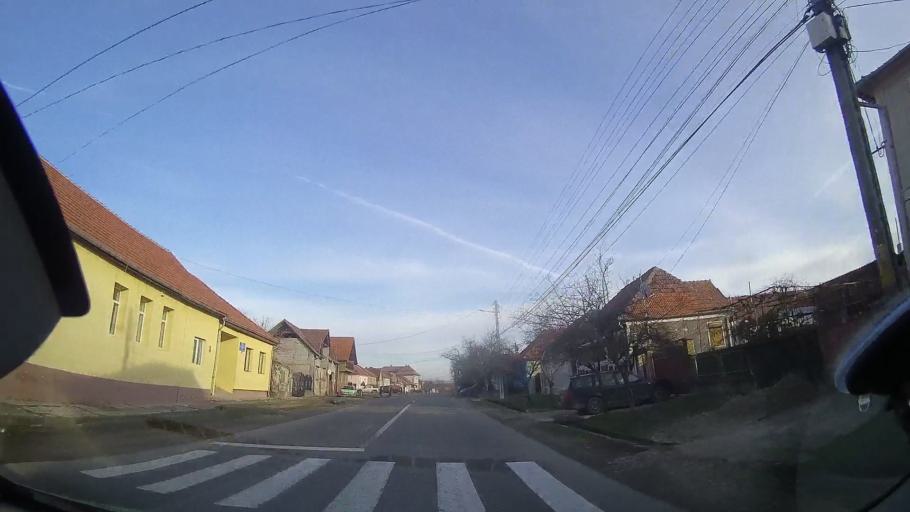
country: RO
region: Bihor
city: Lugasu de Jos
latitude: 47.0456
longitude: 22.3229
